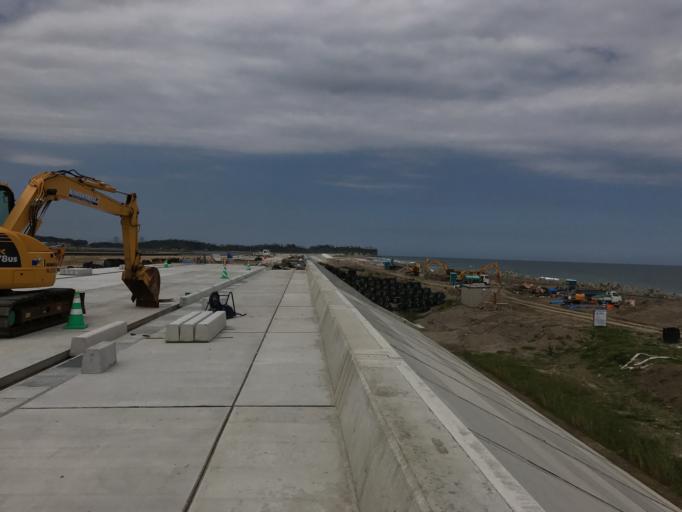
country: JP
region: Miyagi
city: Marumori
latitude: 37.8045
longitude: 140.9858
